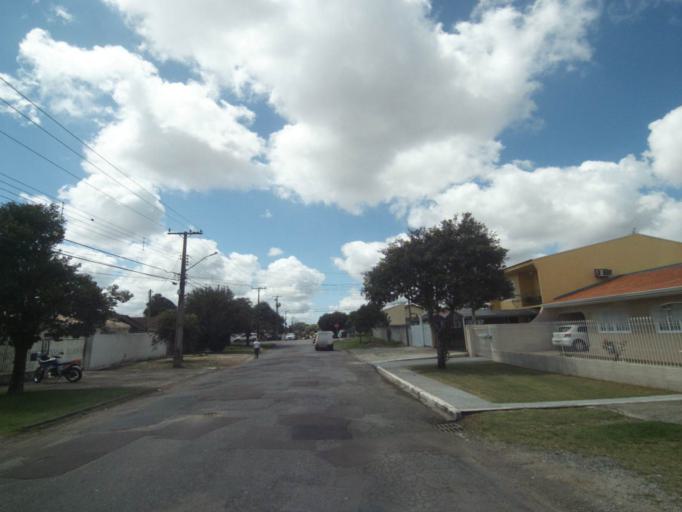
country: BR
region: Parana
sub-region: Pinhais
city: Pinhais
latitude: -25.4421
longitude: -49.2086
